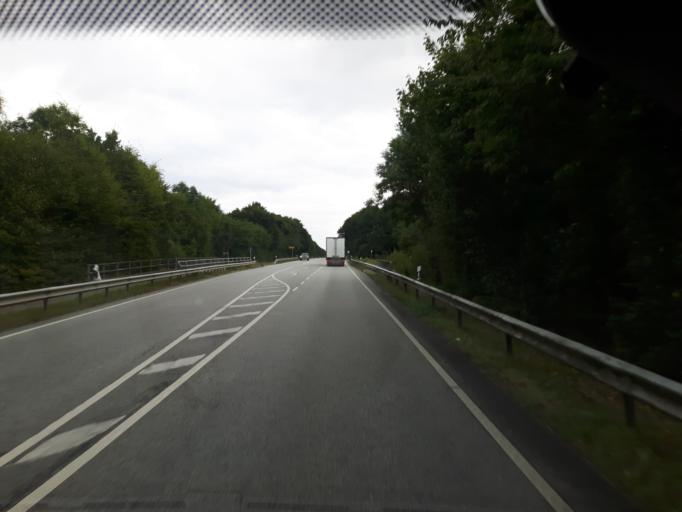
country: DE
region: Schleswig-Holstein
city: Neudorf-Bornstein
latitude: 54.4383
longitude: 9.9283
